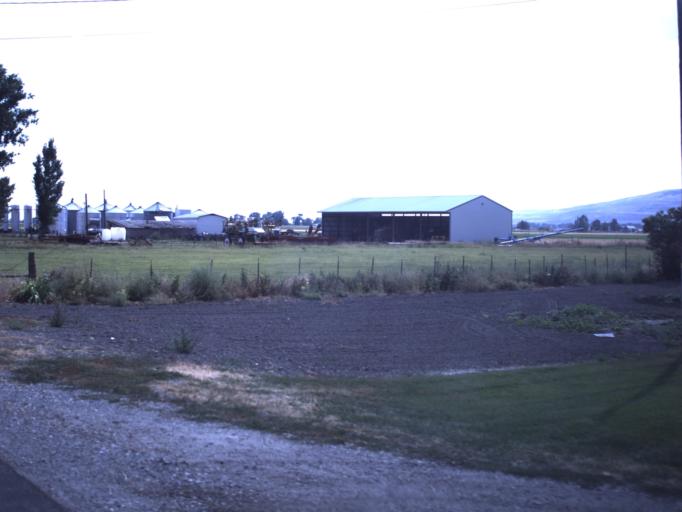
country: US
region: Utah
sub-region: Box Elder County
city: Garland
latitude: 41.8069
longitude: -112.1160
